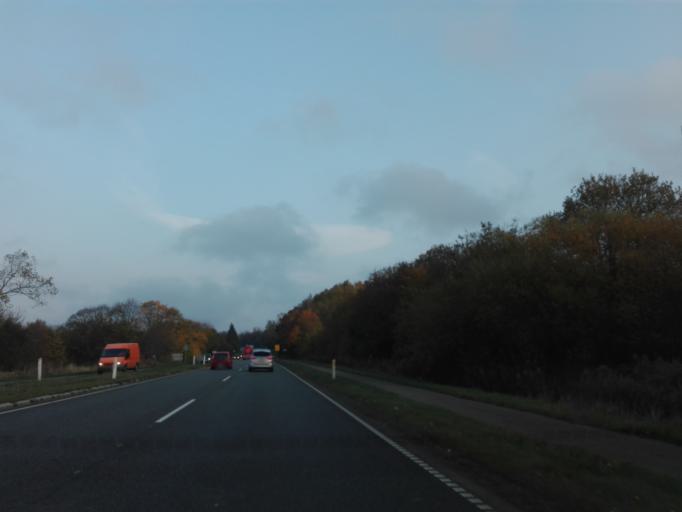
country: DK
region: Central Jutland
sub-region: Arhus Kommune
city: Beder
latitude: 56.0941
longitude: 10.2097
